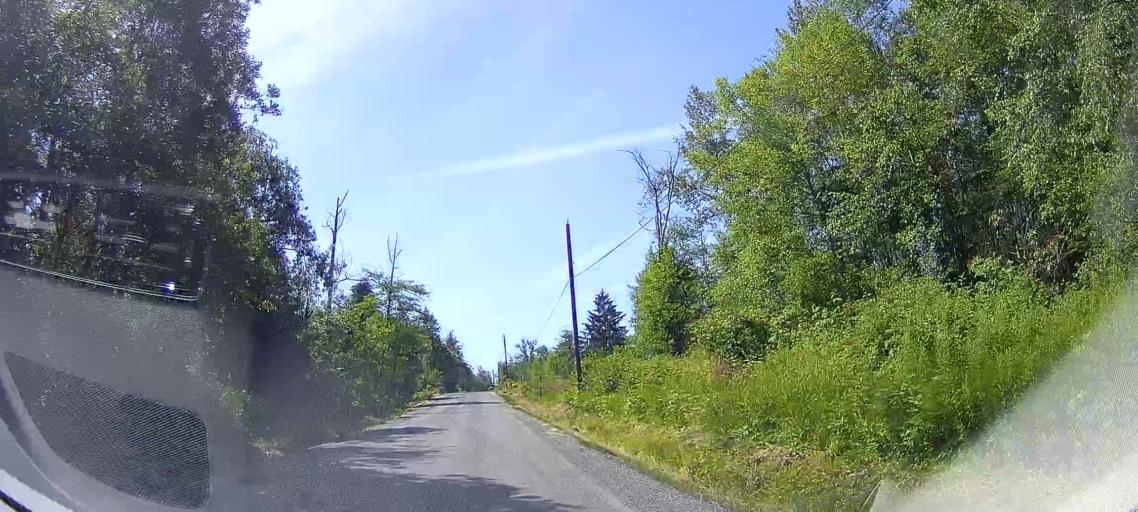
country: US
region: Washington
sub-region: Skagit County
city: Sedro-Woolley
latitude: 48.5404
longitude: -122.2484
